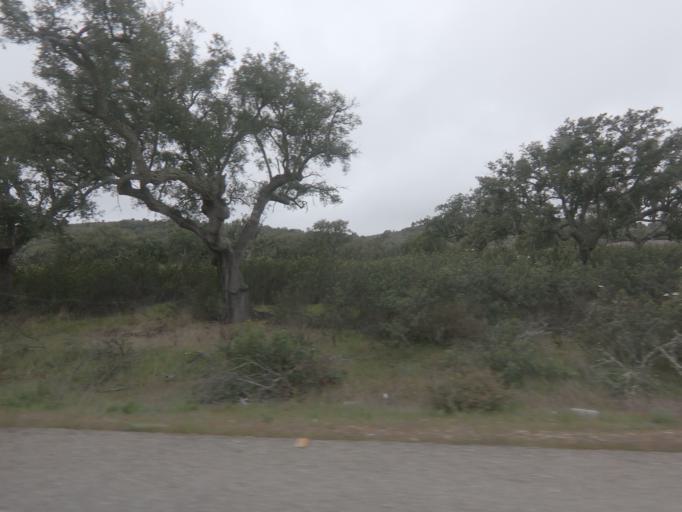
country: ES
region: Extremadura
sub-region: Provincia de Badajoz
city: Puebla de Obando
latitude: 39.2782
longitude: -6.5206
